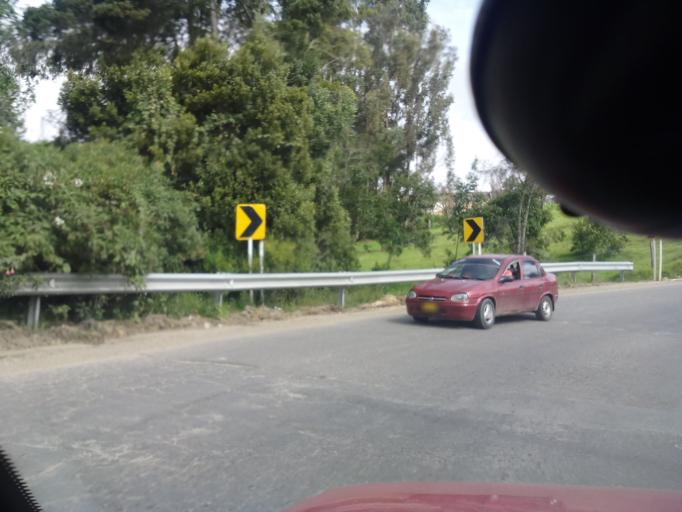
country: CO
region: Boyaca
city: Combita
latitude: 5.6320
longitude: -73.3207
